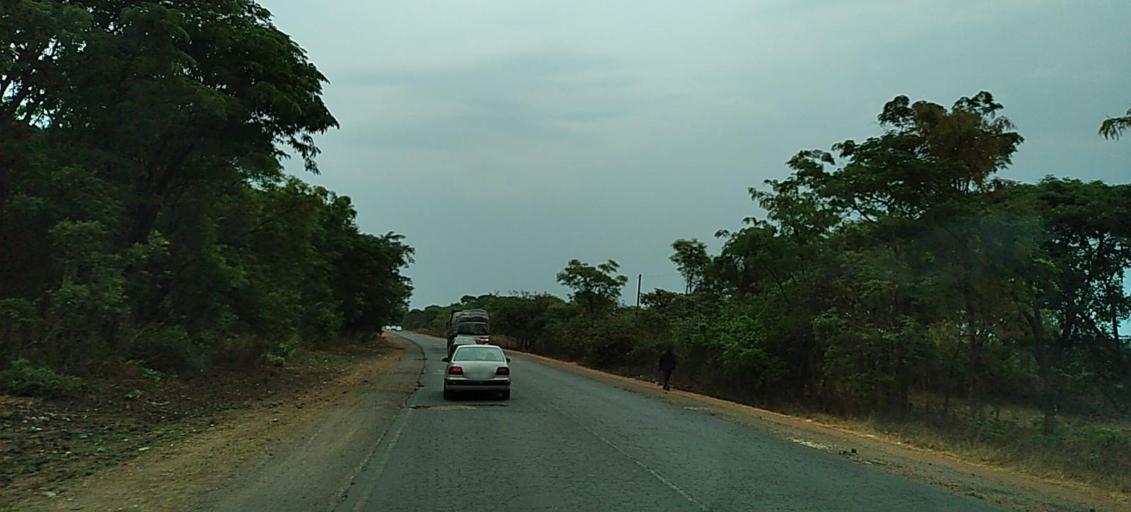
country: ZM
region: Copperbelt
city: Luanshya
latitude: -13.0858
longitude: 28.4386
